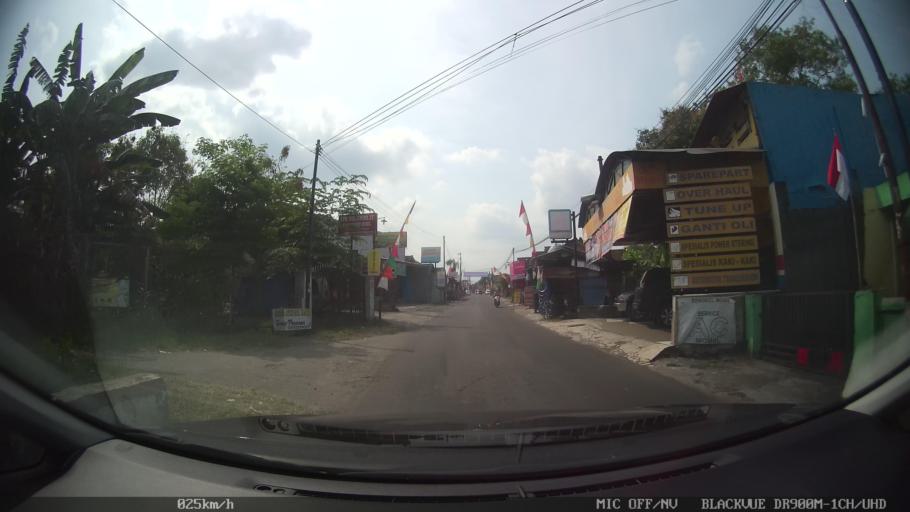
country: ID
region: Daerah Istimewa Yogyakarta
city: Depok
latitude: -7.7877
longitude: 110.4478
